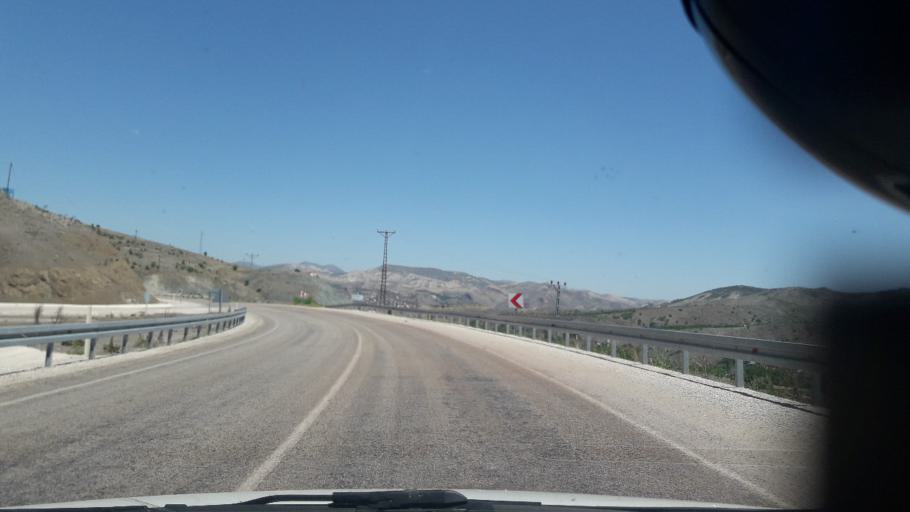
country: TR
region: Malatya
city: Hekimhan
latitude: 38.8216
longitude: 37.8739
